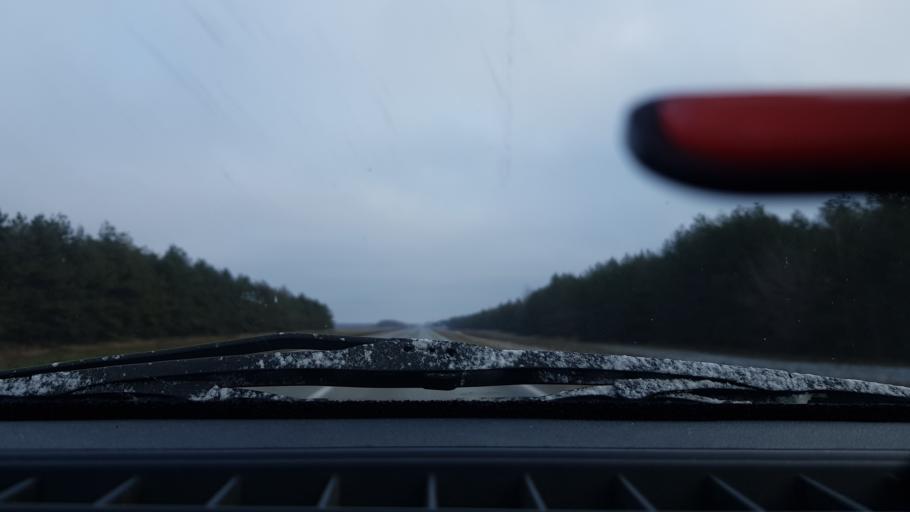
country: RU
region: Tatarstan
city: Kuybyshevskiy Zaton
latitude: 54.9504
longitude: 49.4621
